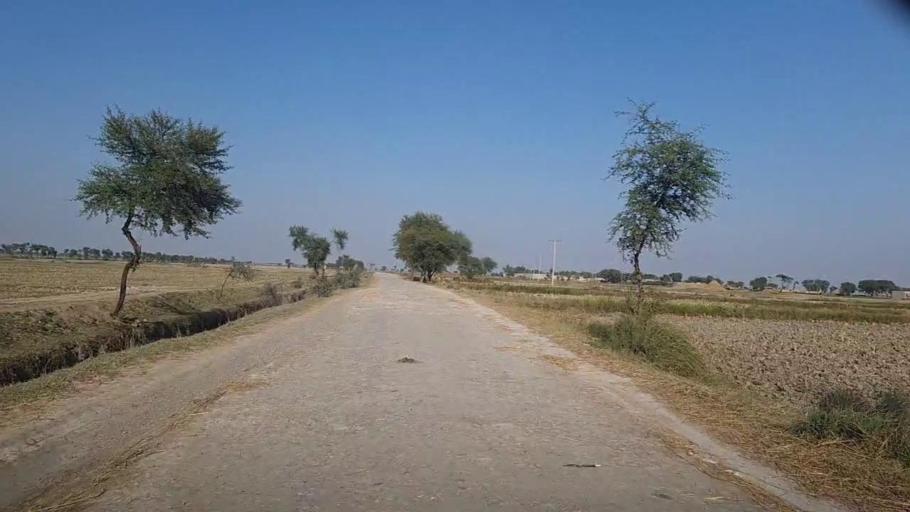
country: PK
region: Sindh
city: Thul
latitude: 28.3521
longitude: 68.7636
